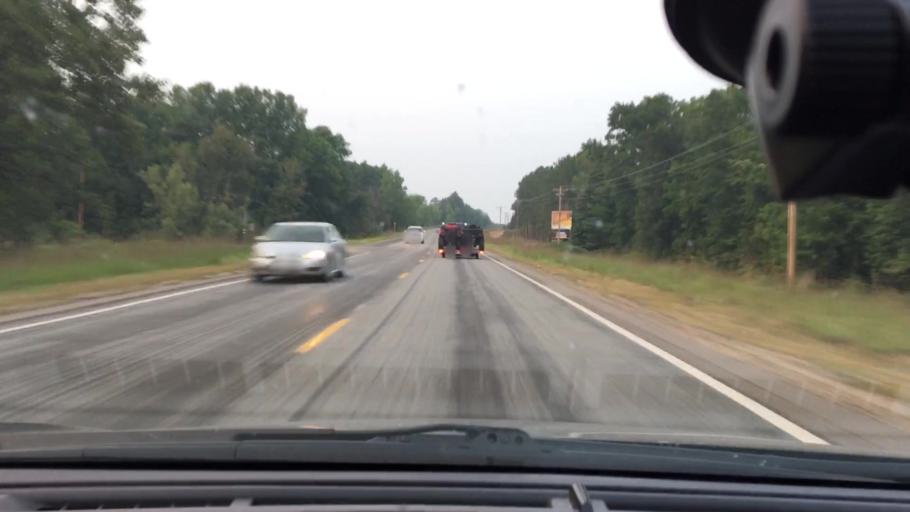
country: US
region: Minnesota
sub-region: Crow Wing County
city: Cross Lake
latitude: 46.8075
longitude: -93.9515
